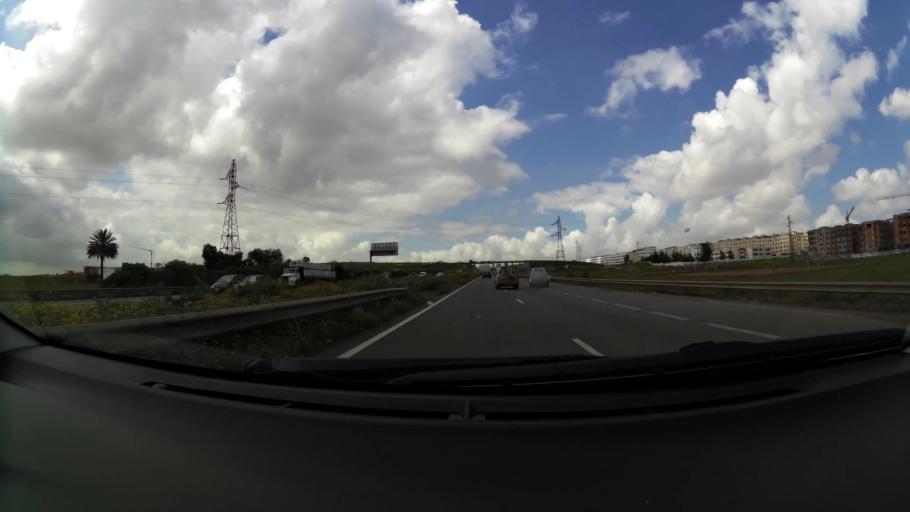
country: MA
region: Grand Casablanca
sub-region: Mediouna
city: Tit Mellil
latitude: 33.5364
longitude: -7.5449
